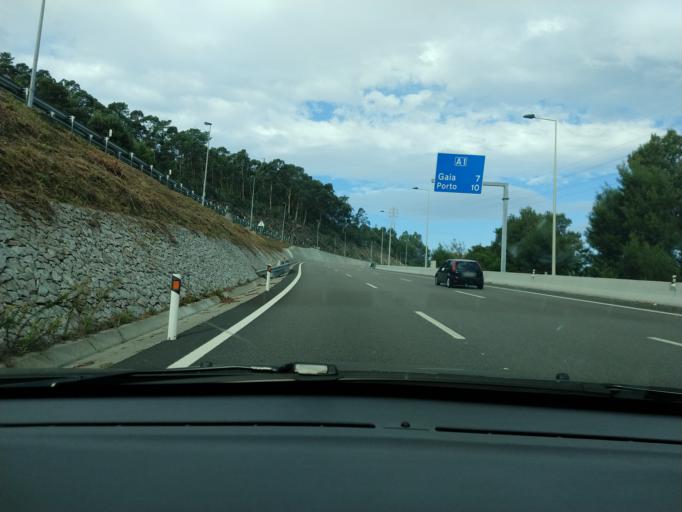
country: PT
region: Porto
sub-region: Vila Nova de Gaia
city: Perozinho
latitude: 41.0779
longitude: -8.5794
